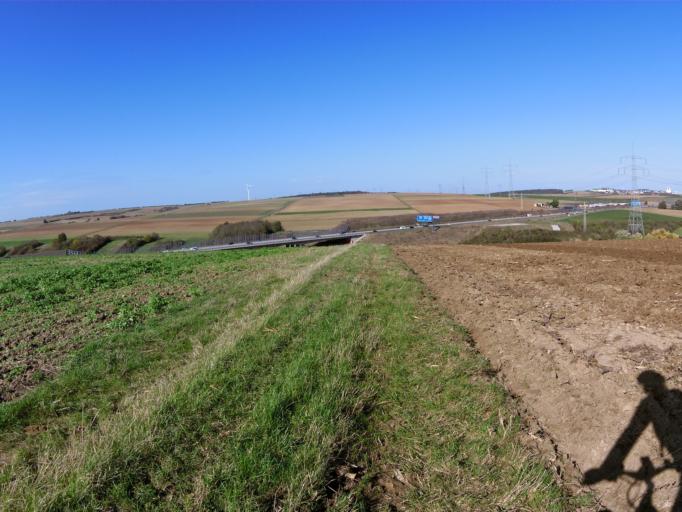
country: DE
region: Bavaria
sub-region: Regierungsbezirk Unterfranken
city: Theilheim
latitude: 49.7531
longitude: 10.0520
